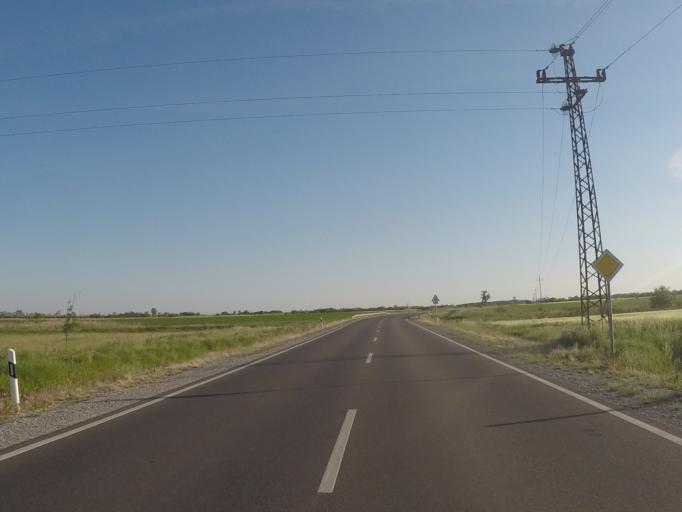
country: HU
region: Heves
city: Besenyotelek
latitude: 47.6847
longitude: 20.3870
